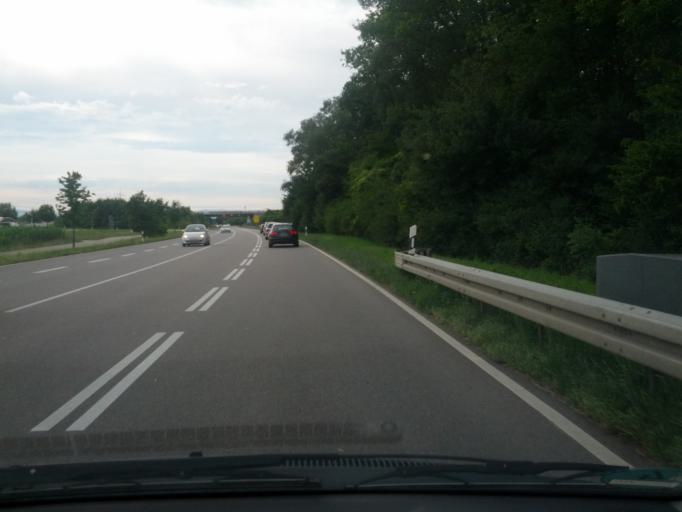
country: DE
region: Baden-Wuerttemberg
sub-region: Freiburg Region
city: Rust
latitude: 48.2578
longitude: 7.7517
